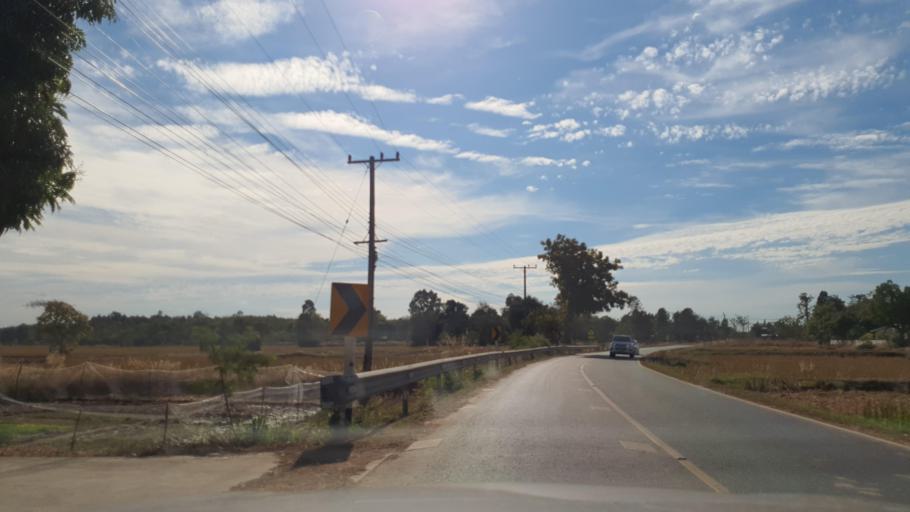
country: TH
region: Kalasin
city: Kuchinarai
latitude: 16.5435
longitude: 104.0925
